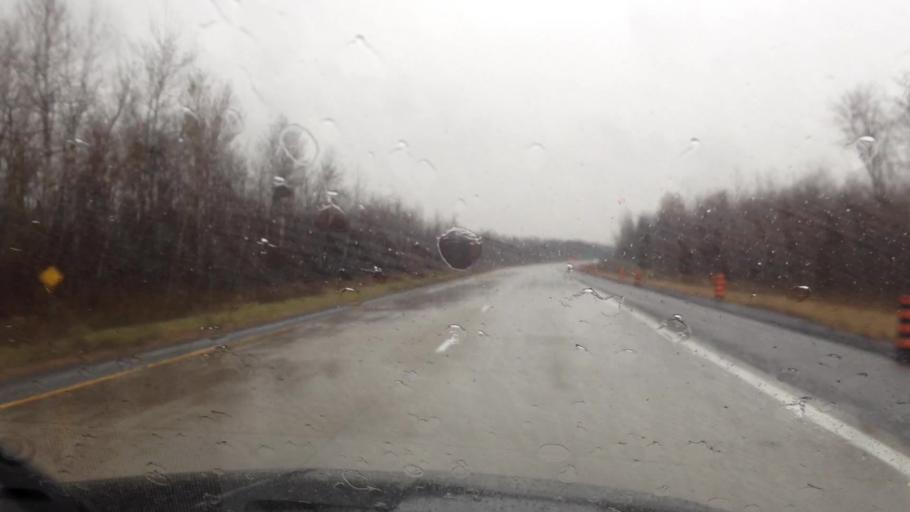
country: CA
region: Ontario
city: Hawkesbury
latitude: 45.4588
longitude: -74.6913
